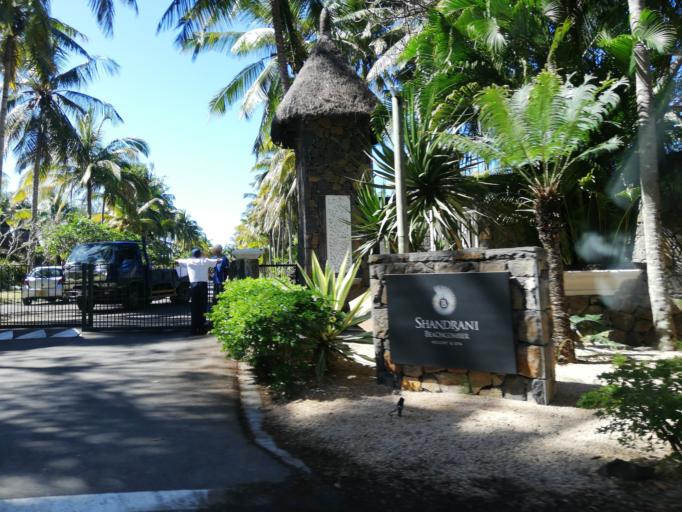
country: MU
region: Grand Port
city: Beau Vallon
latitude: -20.4476
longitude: 57.7036
